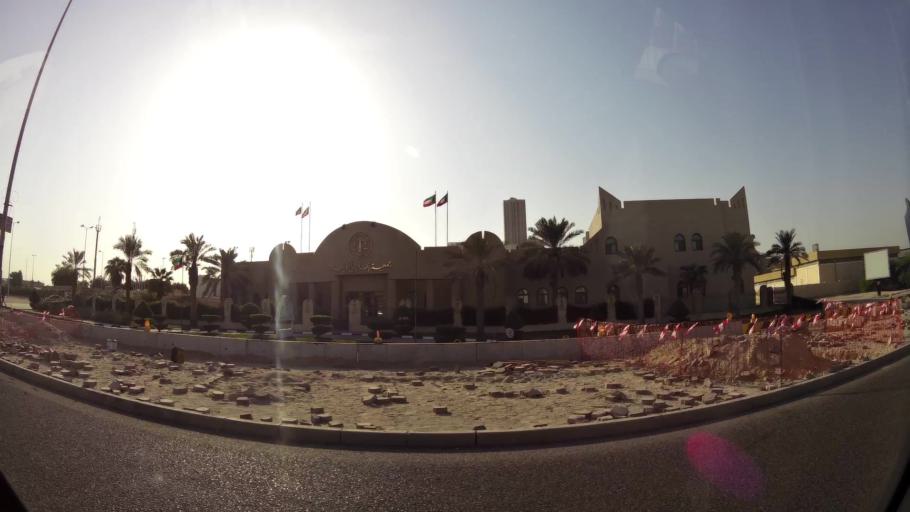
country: KW
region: Al Asimah
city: Ad Dasmah
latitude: 29.3814
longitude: 47.9989
